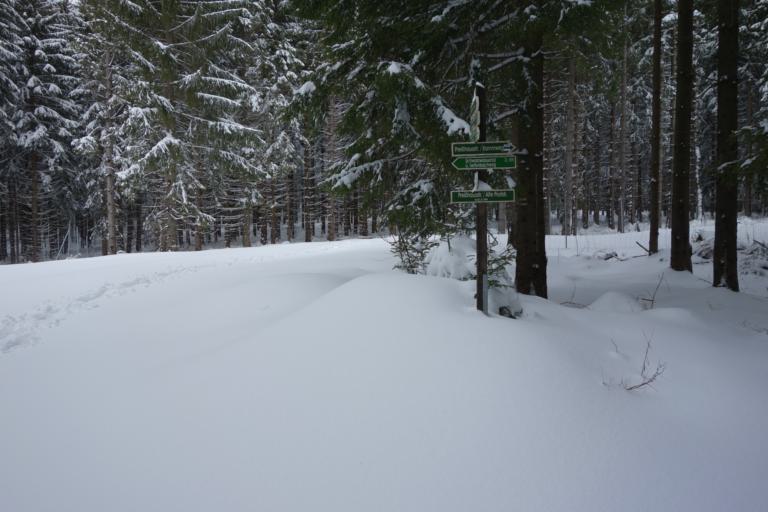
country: DE
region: Saxony
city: Breitenbrunn
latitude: 50.4416
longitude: 12.7543
